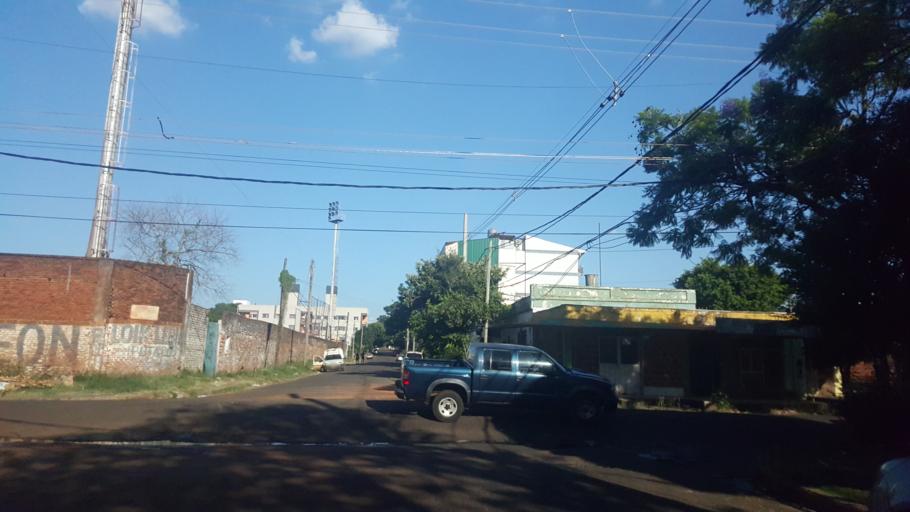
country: AR
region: Misiones
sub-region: Departamento de Capital
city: Posadas
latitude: -27.3862
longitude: -55.8994
